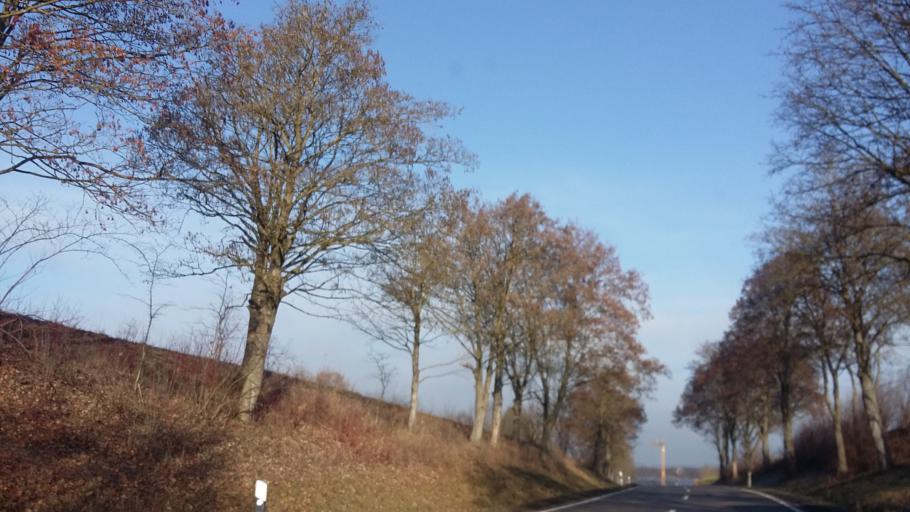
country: DE
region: Bavaria
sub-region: Swabia
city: Sielenbach
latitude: 48.3750
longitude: 11.1591
